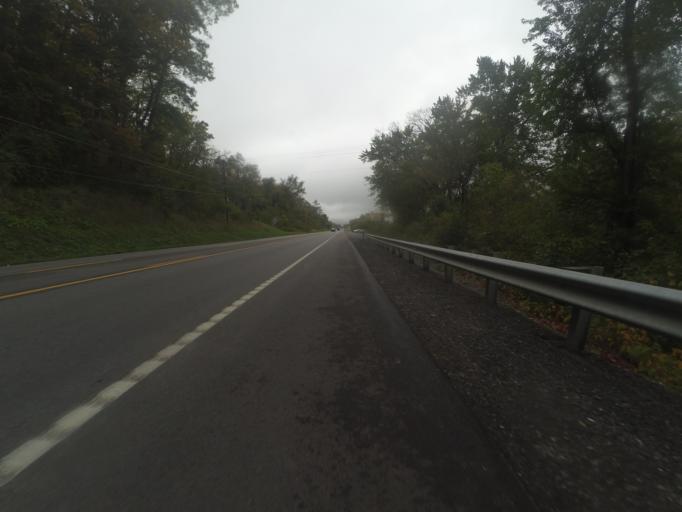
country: US
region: Pennsylvania
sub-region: Huntingdon County
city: McConnellstown
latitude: 40.5412
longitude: -78.0900
